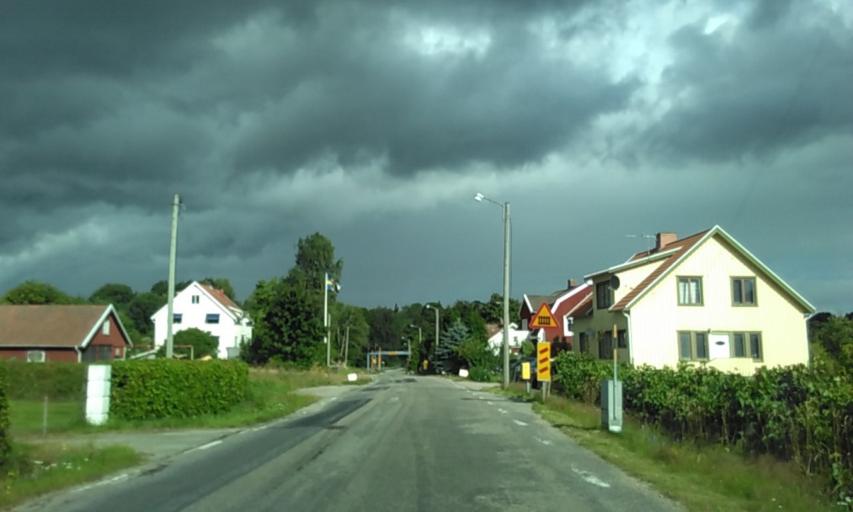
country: SE
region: Vaestra Goetaland
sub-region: Vargarda Kommun
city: Jonstorp
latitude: 58.0074
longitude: 12.7102
